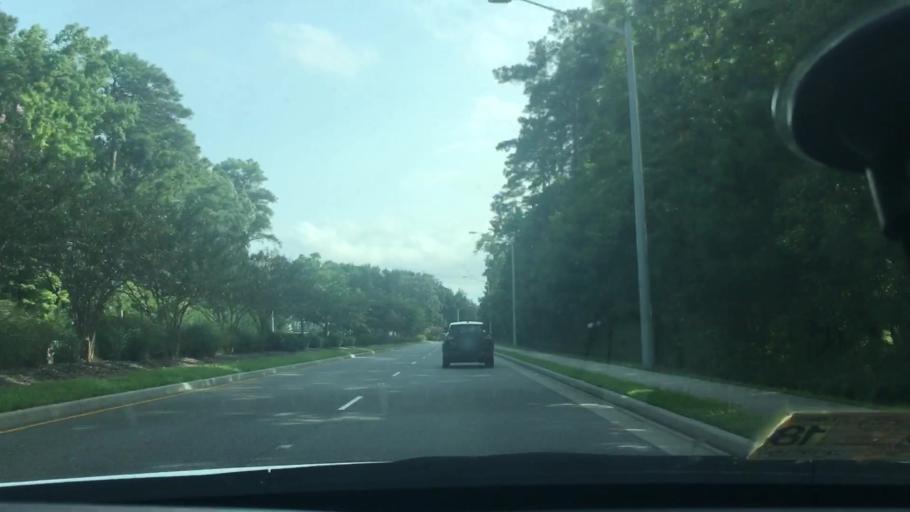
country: US
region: Virginia
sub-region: City of Virginia Beach
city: Virginia Beach
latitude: 36.8267
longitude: -75.9977
